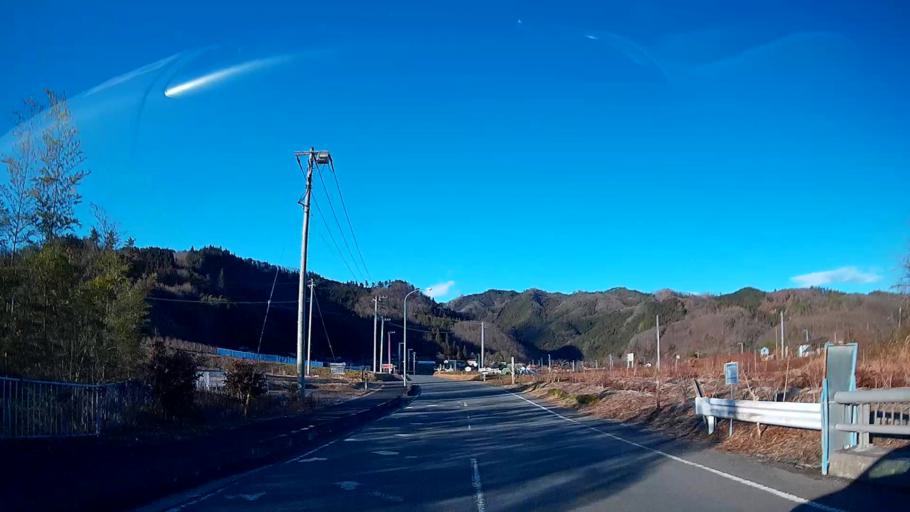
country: JP
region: Saitama
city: Chichibu
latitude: 36.0389
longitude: 139.0108
